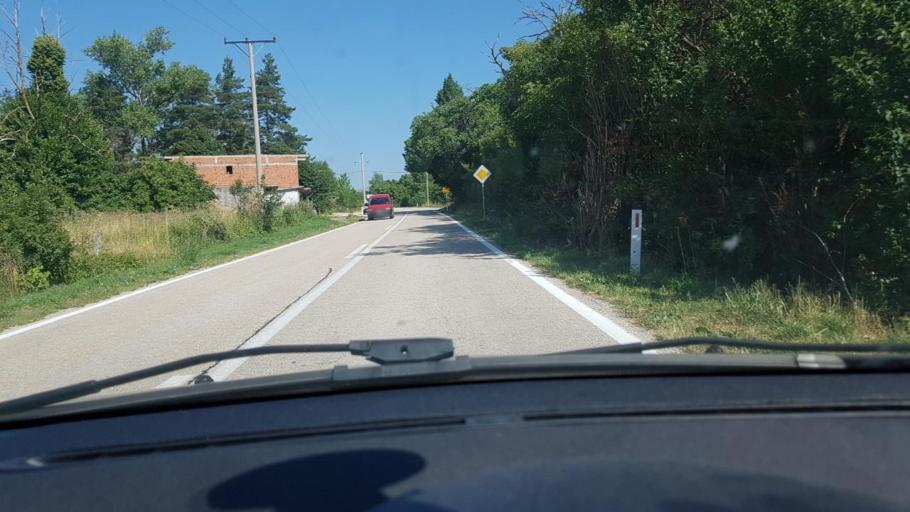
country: BA
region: Federation of Bosnia and Herzegovina
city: Bosansko Grahovo
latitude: 44.0909
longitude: 16.5642
